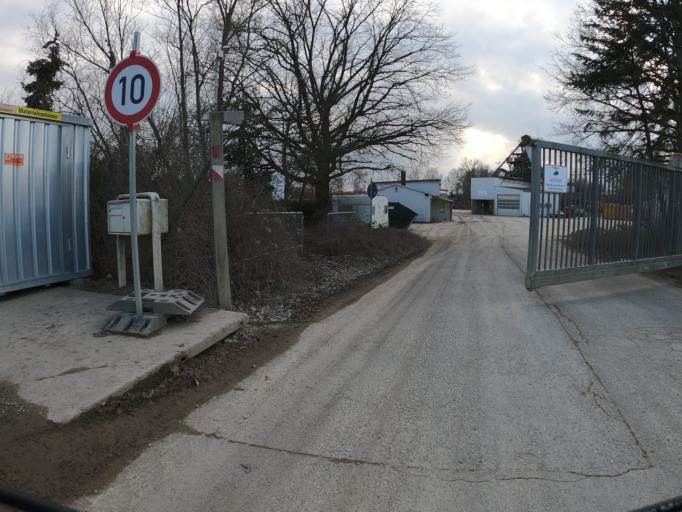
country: DE
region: Bavaria
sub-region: Swabia
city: Nersingen
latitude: 48.4508
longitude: 10.1131
